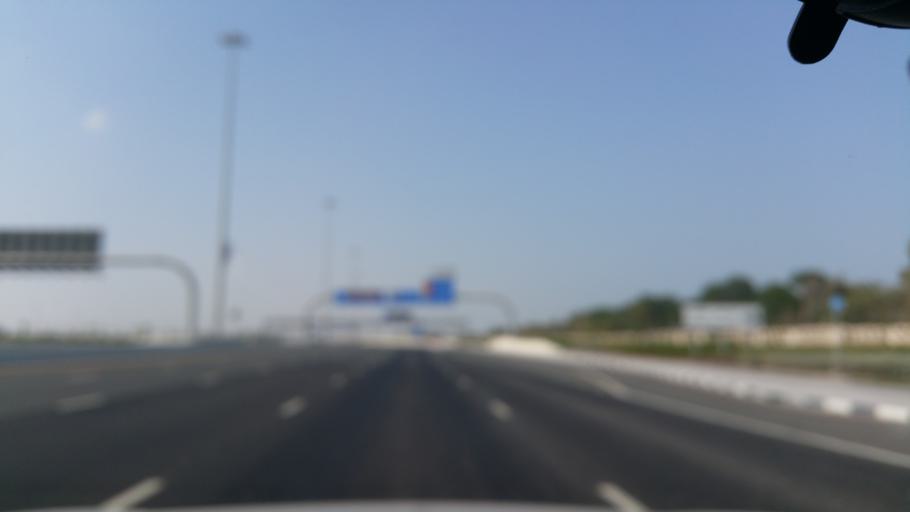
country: QA
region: Baladiyat Umm Salal
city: Umm Salal Muhammad
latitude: 25.3815
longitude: 51.5003
